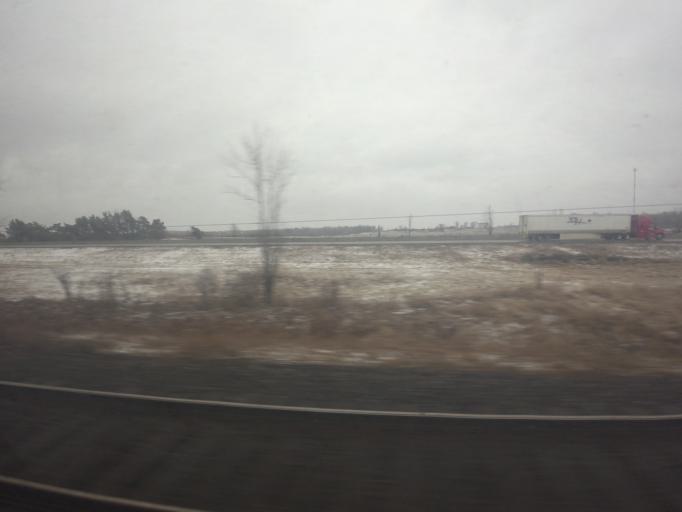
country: CA
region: Ontario
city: Kingston
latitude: 44.3208
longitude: -76.3558
